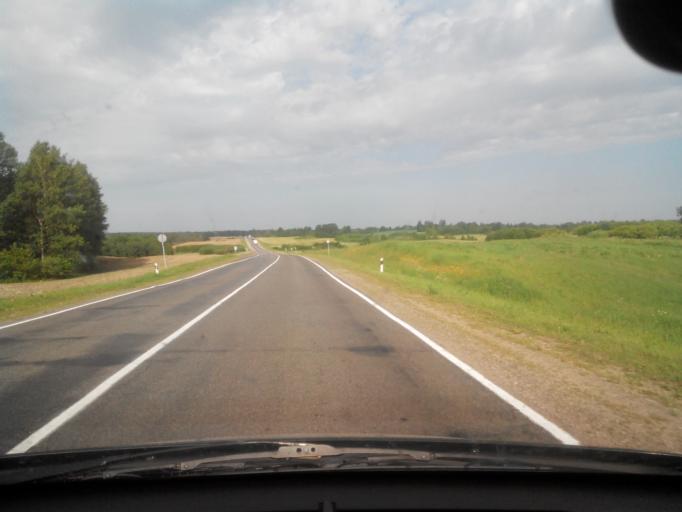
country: BY
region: Minsk
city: Myadzyel
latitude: 55.0642
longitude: 27.1868
